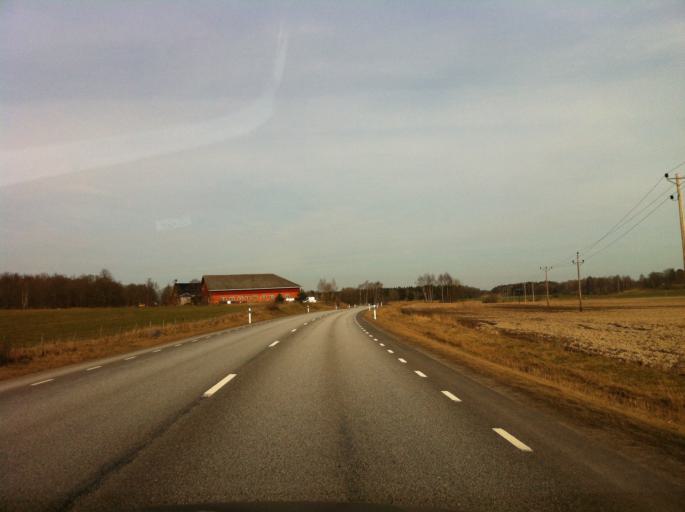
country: SE
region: Vaestra Goetaland
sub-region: Mariestads Kommun
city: Mariestad
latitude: 58.7665
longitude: 13.9507
